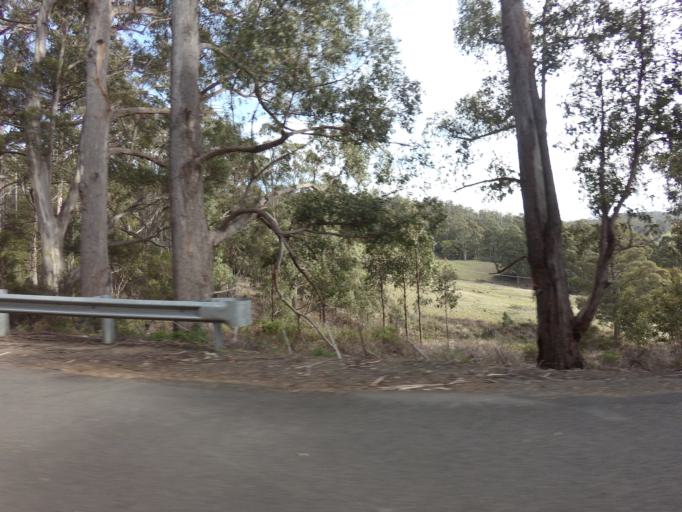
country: AU
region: Tasmania
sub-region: Kingborough
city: Margate
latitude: -43.0068
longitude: 147.1692
